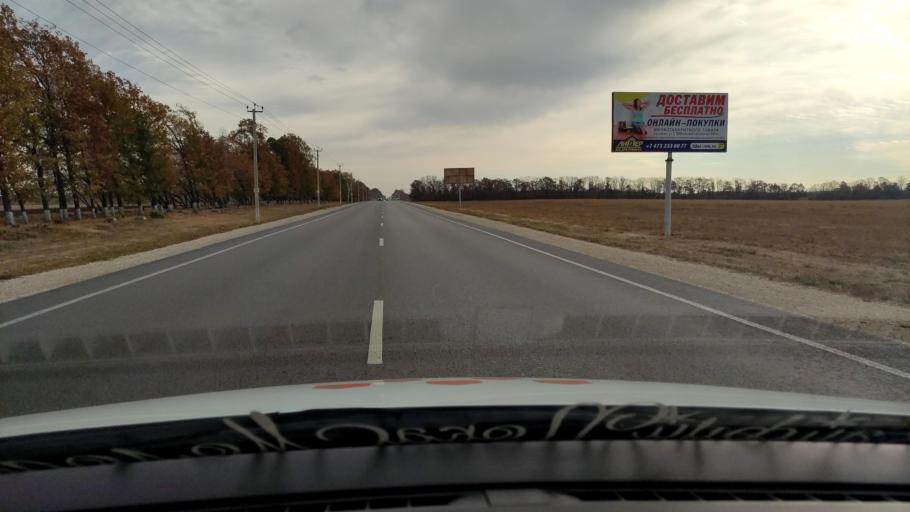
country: RU
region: Voronezj
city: Ramon'
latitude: 51.9284
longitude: 39.2350
